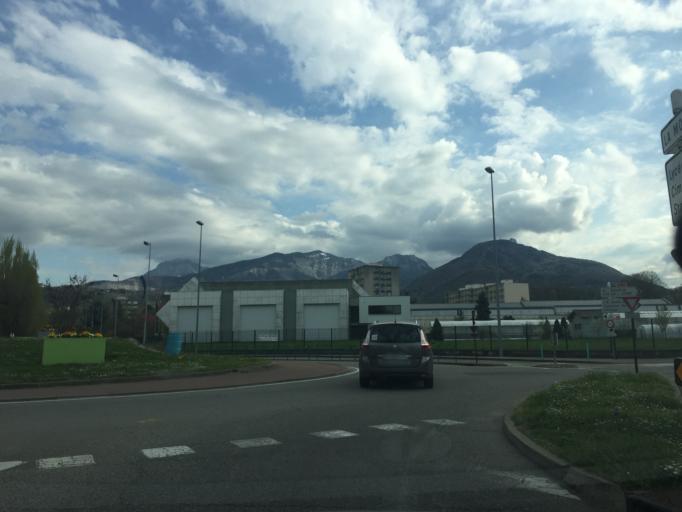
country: FR
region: Rhone-Alpes
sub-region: Departement de la Savoie
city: Cognin
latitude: 45.5626
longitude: 5.8937
